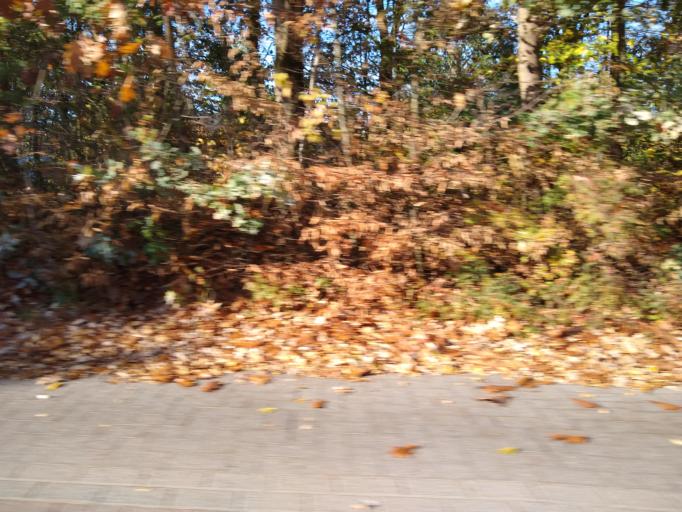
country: DE
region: Lower Saxony
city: Oldenburg
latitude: 53.1882
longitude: 8.2022
